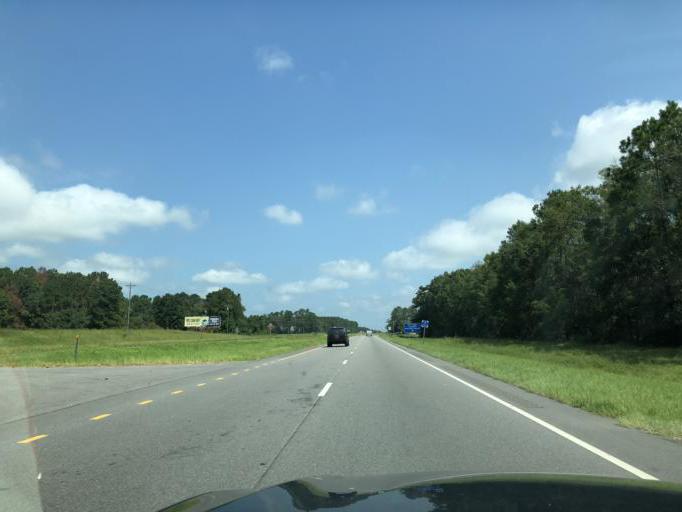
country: US
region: Alabama
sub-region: Houston County
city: Cottonwood
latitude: 31.0047
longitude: -85.4077
